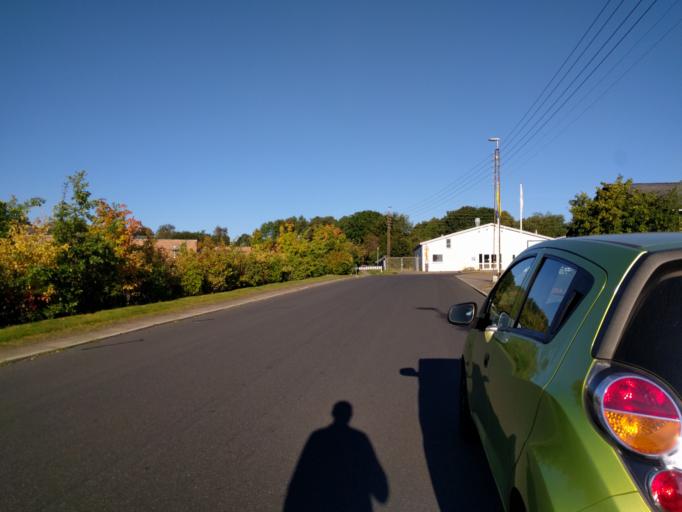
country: DK
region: Central Jutland
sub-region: Silkeborg Kommune
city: Silkeborg
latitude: 56.1838
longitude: 9.5334
